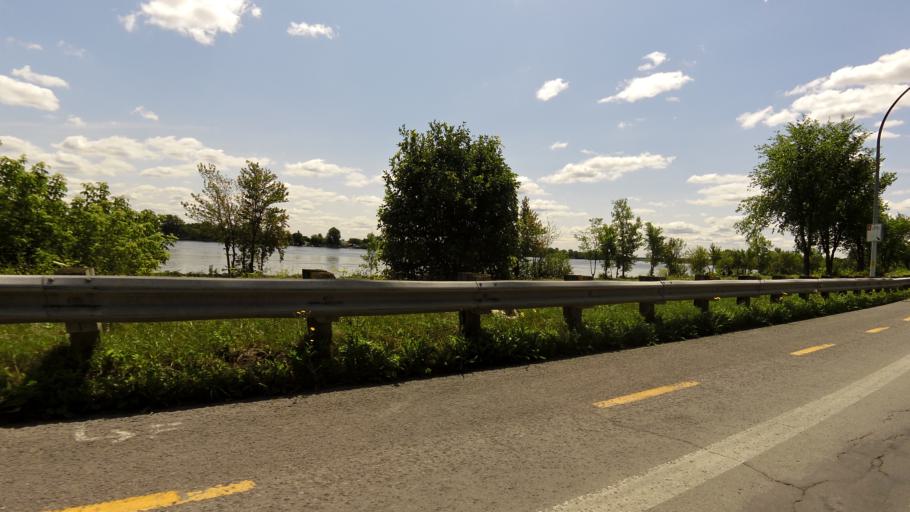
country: CA
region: Quebec
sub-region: Monteregie
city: Saint-Jean-sur-Richelieu
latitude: 45.3438
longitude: -73.2663
